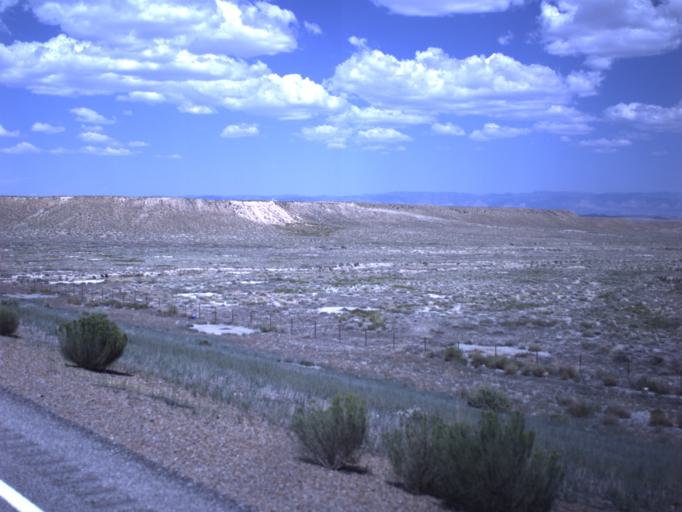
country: US
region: Utah
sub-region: Carbon County
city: Price
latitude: 39.4708
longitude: -110.8562
